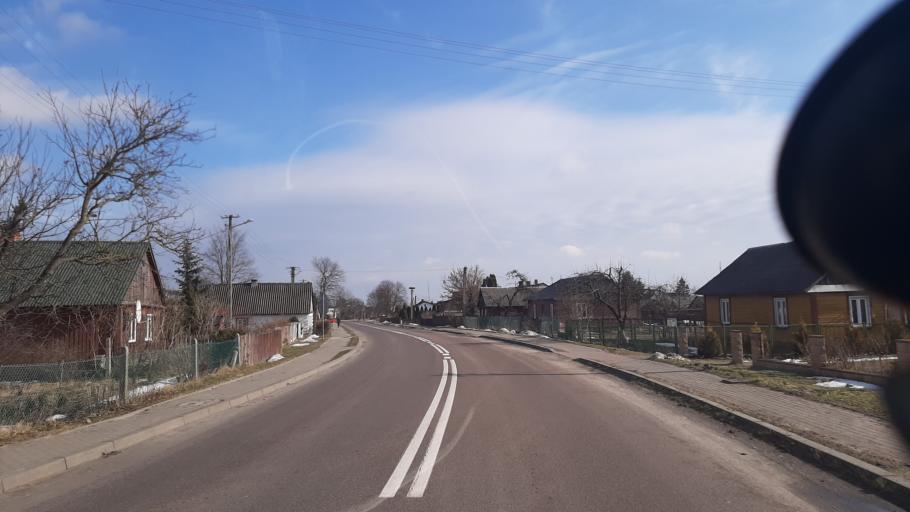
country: PL
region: Lublin Voivodeship
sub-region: Powiat wlodawski
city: Hansk
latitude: 51.4807
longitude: 23.2923
